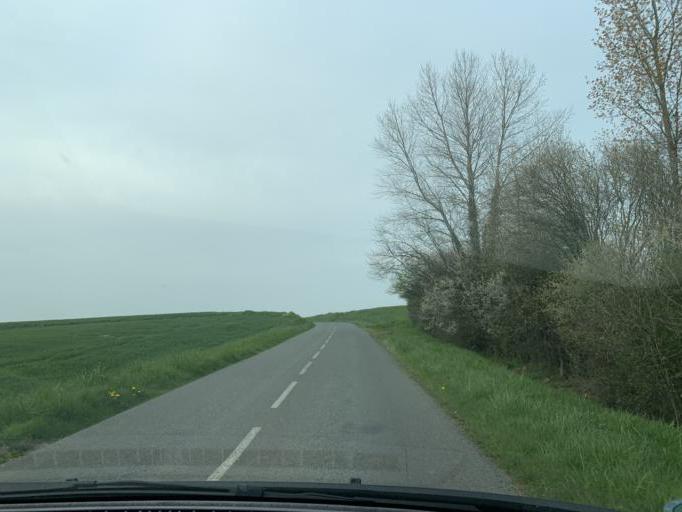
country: FR
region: Nord-Pas-de-Calais
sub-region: Departement du Pas-de-Calais
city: Samer
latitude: 50.6515
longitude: 1.7521
